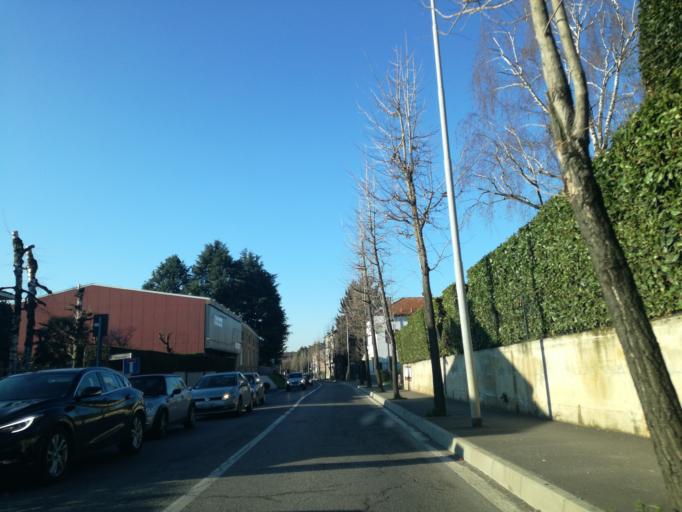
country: IT
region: Lombardy
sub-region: Provincia di Monza e Brianza
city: Bernareggio
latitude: 45.6528
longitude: 9.4095
